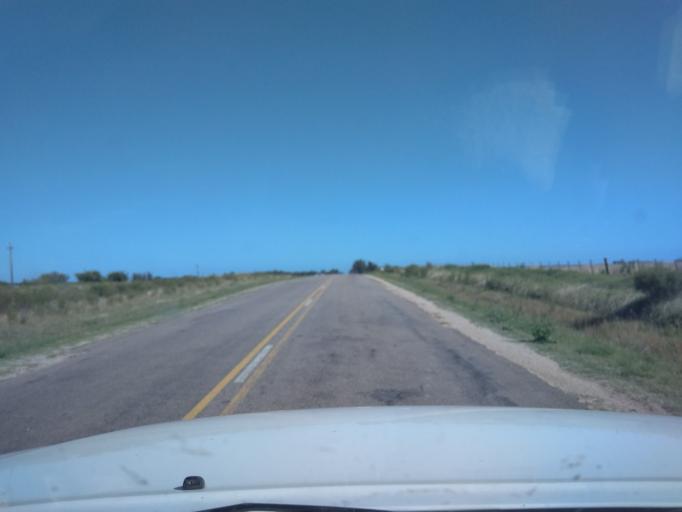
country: UY
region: Canelones
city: San Ramon
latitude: -34.2088
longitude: -55.9304
